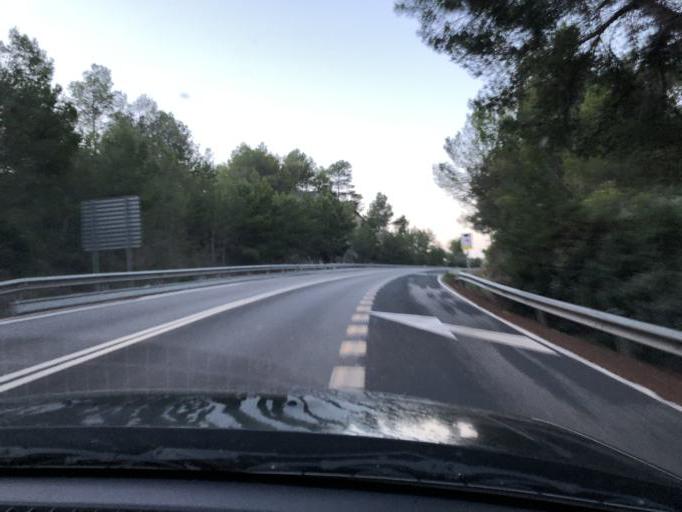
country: ES
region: Balearic Islands
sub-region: Illes Balears
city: Andratx
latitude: 39.5618
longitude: 2.4228
